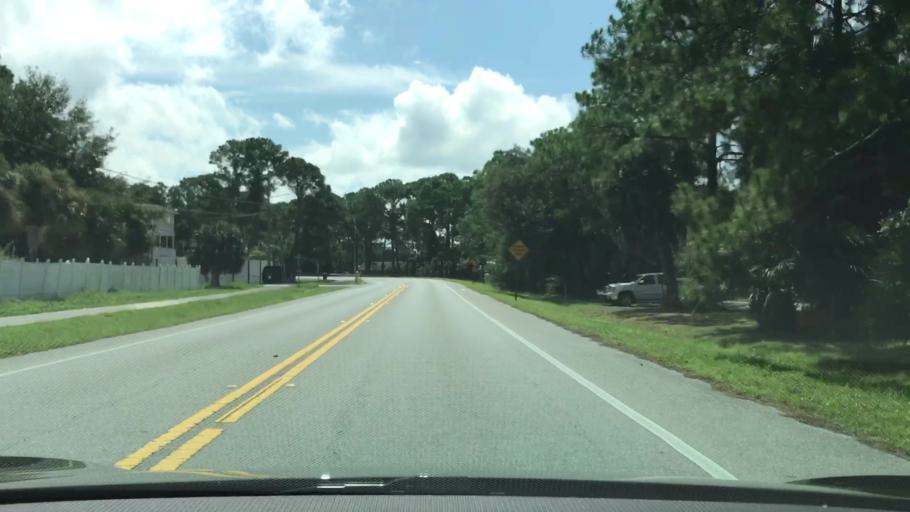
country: US
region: Florida
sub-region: Bay County
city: Lower Grand Lagoon
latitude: 30.1543
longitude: -85.7543
